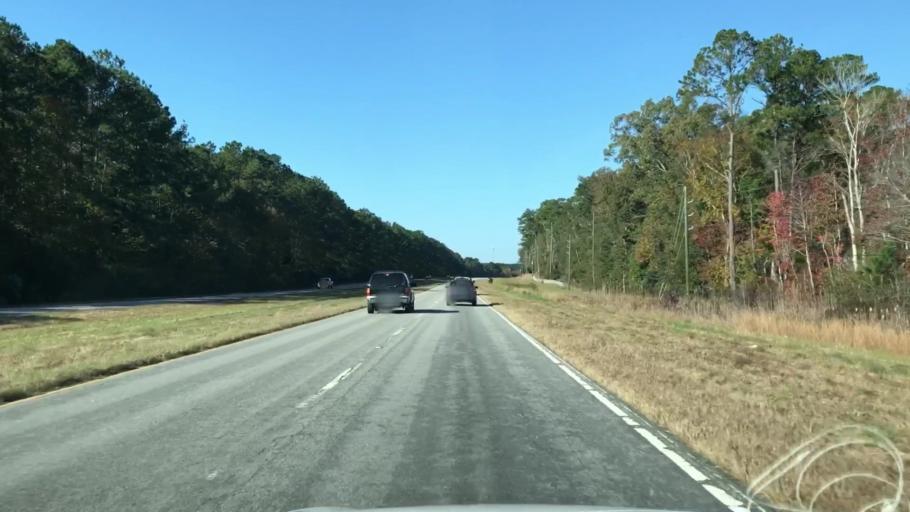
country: US
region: South Carolina
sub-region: Charleston County
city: Ravenel
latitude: 32.7573
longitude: -80.3725
